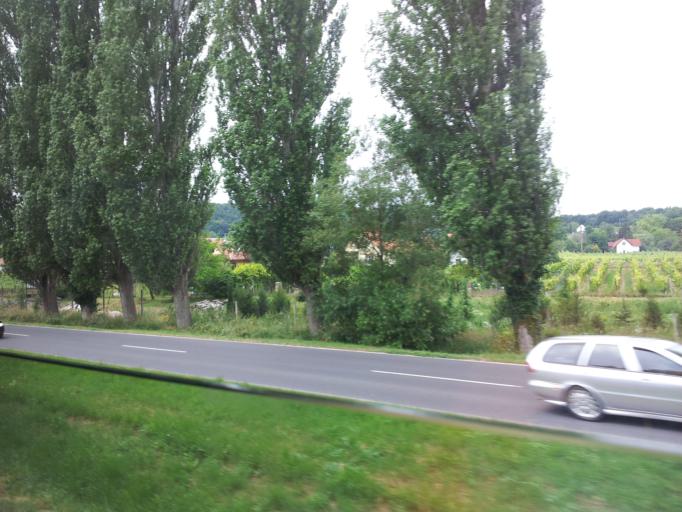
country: HU
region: Veszprem
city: Badacsonytomaj
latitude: 46.8098
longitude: 17.5597
